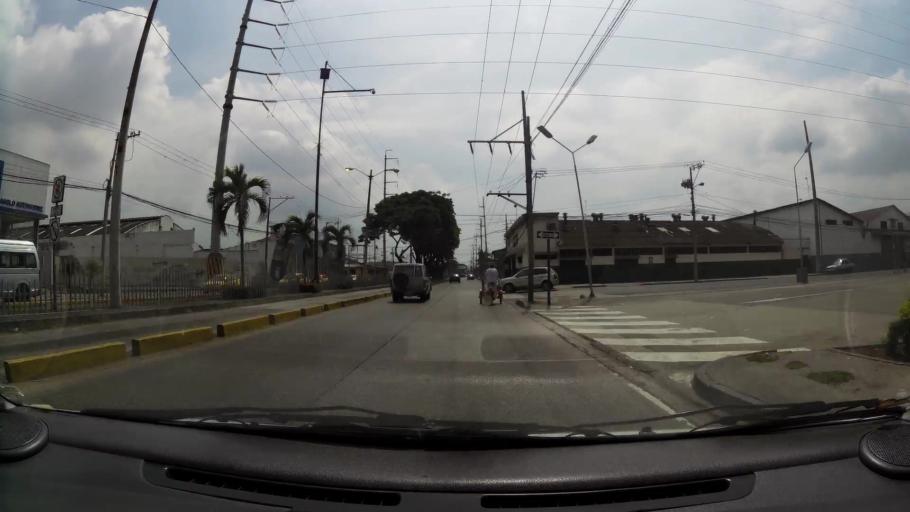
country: EC
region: Guayas
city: Guayaquil
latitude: -2.2366
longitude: -79.8909
